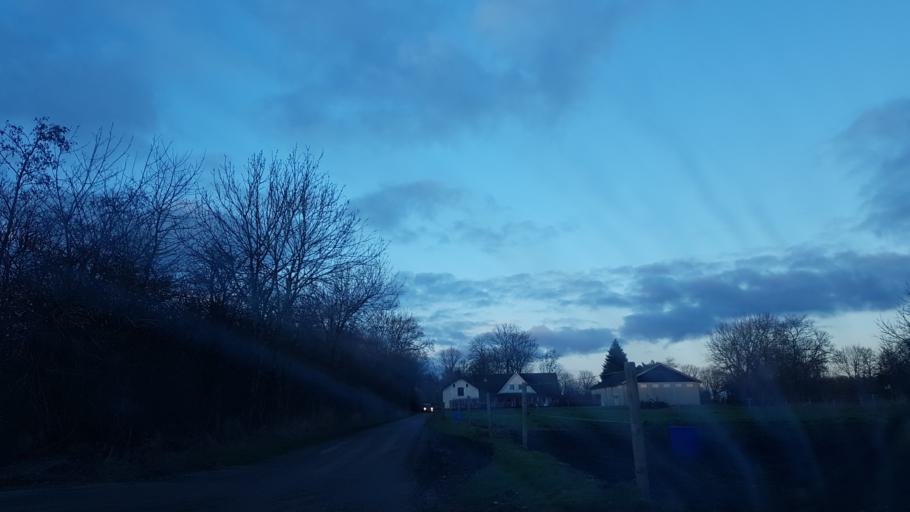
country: DK
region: South Denmark
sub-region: Kolding Kommune
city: Vamdrup
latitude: 55.3453
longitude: 9.2493
